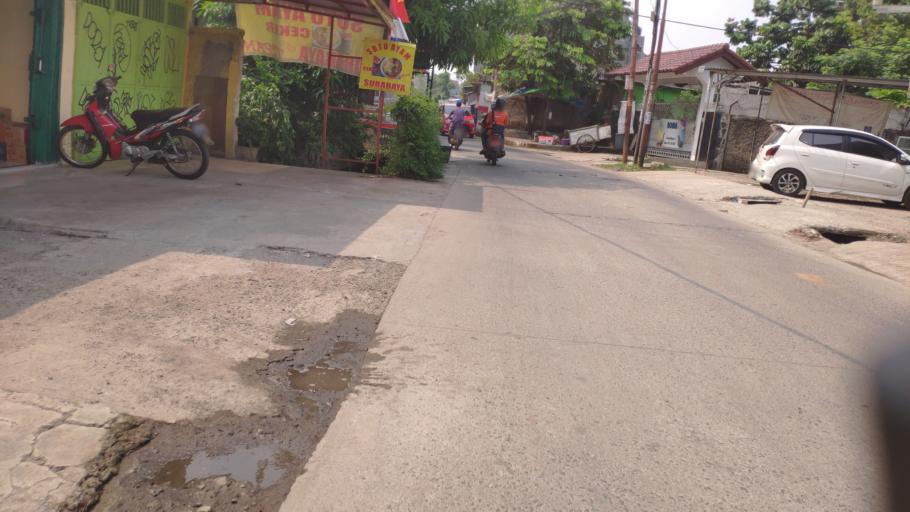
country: ID
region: West Java
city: Depok
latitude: -6.3833
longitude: 106.8041
